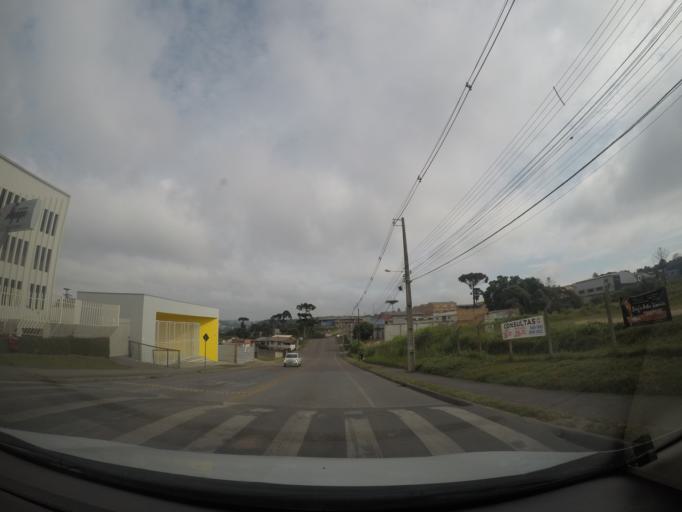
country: BR
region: Parana
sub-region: Colombo
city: Colombo
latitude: -25.3459
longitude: -49.2211
